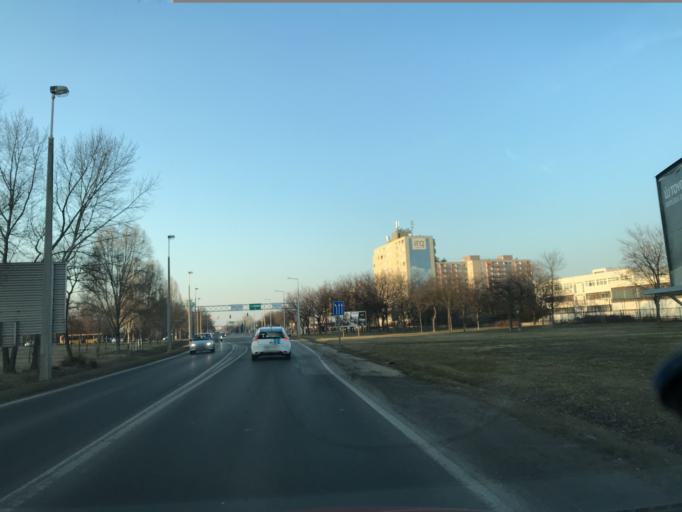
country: HU
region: Gyor-Moson-Sopron
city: Gyor
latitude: 47.6622
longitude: 17.6374
